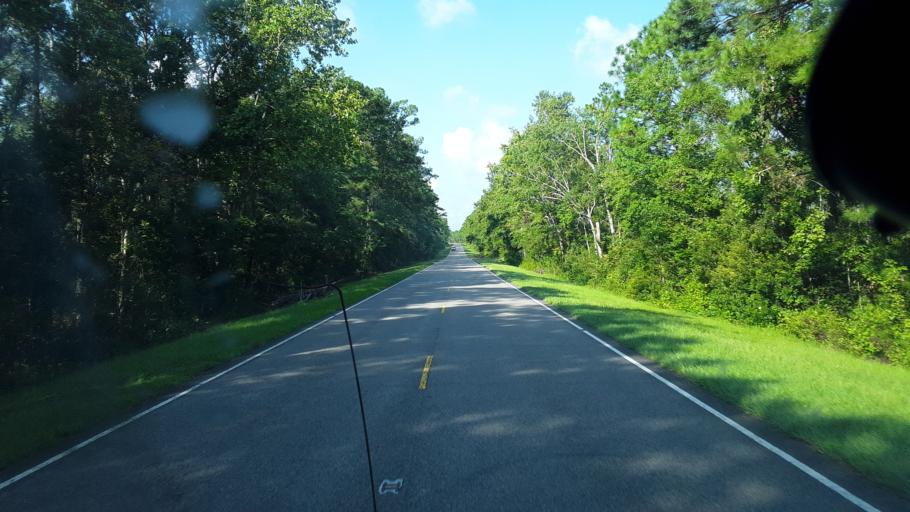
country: US
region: North Carolina
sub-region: Brunswick County
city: Boiling Spring Lakes
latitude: 34.0540
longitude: -77.9862
